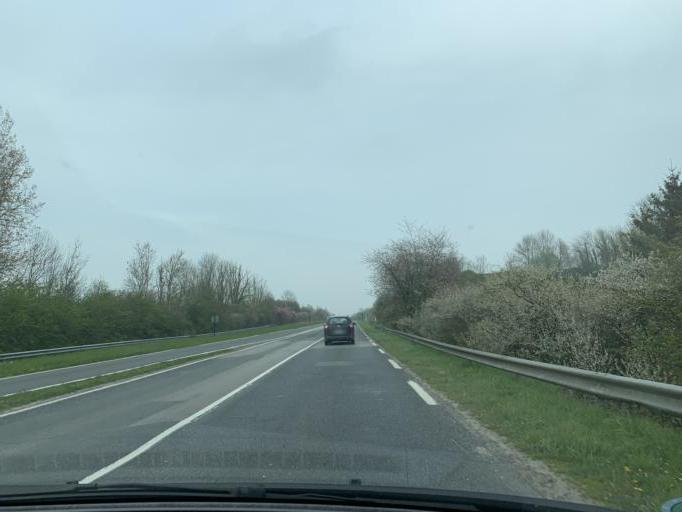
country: FR
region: Nord-Pas-de-Calais
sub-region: Departement du Pas-de-Calais
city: Montreuil
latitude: 50.4564
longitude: 1.7661
